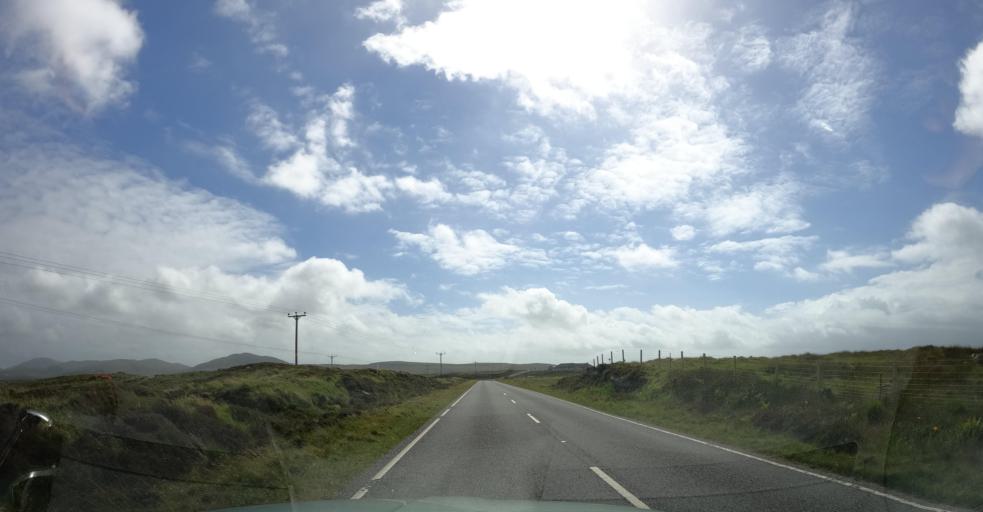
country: GB
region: Scotland
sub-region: Eilean Siar
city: Isle of South Uist
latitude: 57.2539
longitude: -7.3756
